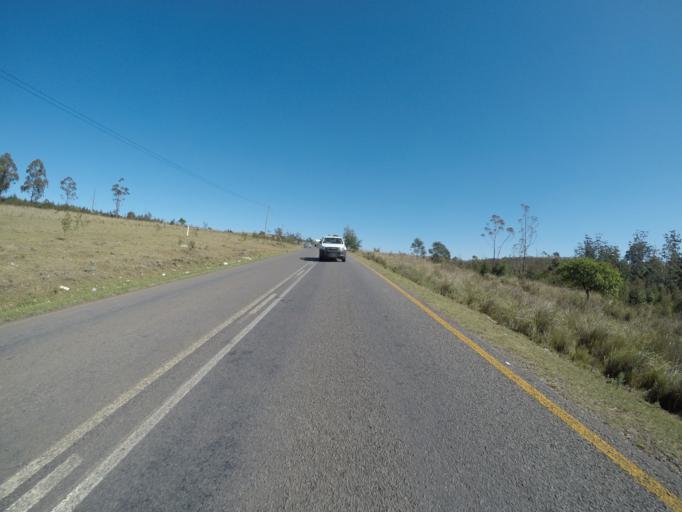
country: ZA
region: Eastern Cape
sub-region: OR Tambo District Municipality
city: Mthatha
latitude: -31.8081
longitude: 28.7634
